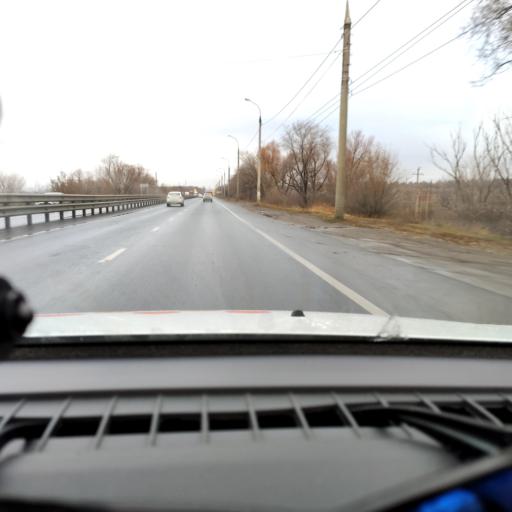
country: RU
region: Samara
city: Samara
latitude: 53.1184
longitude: 50.1677
